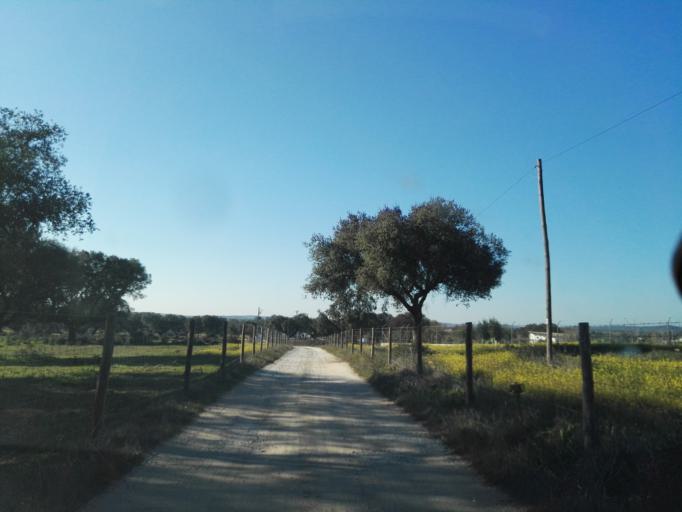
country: PT
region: Evora
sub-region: Evora
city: Evora
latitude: 38.5446
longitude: -7.9490
